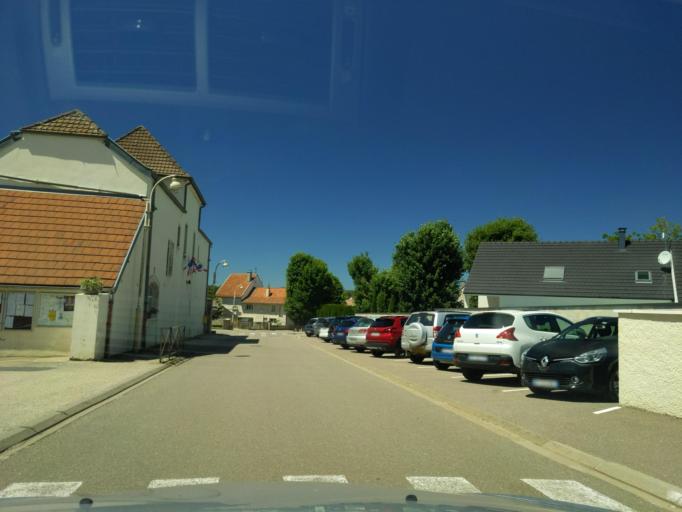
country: FR
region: Bourgogne
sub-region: Departement de la Cote-d'Or
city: Saint-Julien
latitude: 47.4384
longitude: 5.0975
